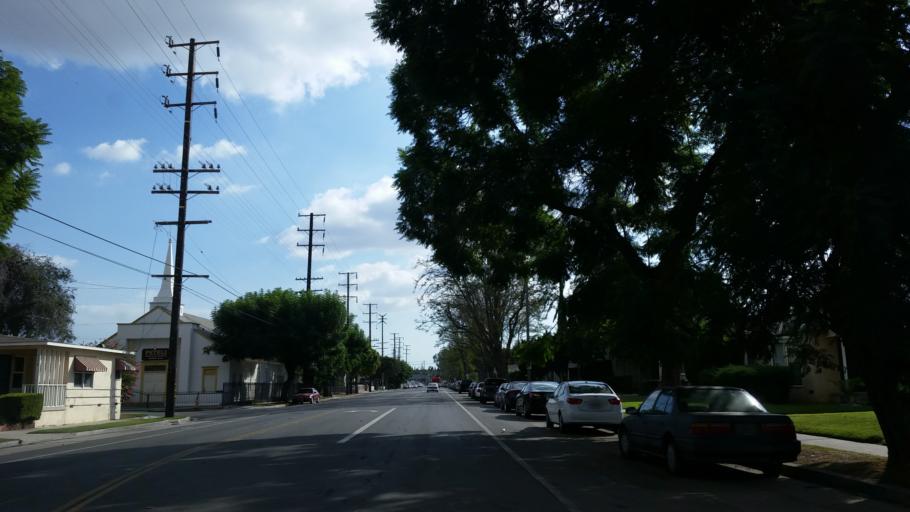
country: US
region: California
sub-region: Los Angeles County
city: Paramount
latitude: 33.8540
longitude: -118.1773
